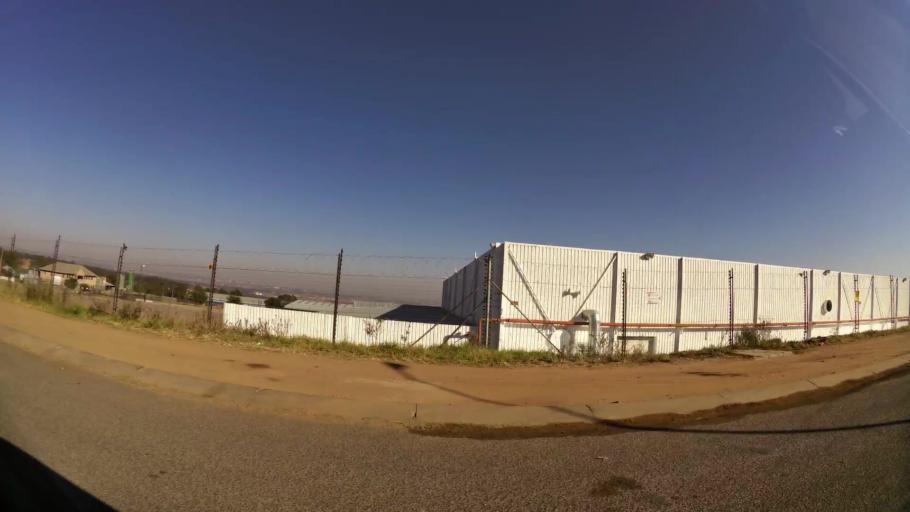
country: ZA
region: Gauteng
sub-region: City of Johannesburg Metropolitan Municipality
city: Modderfontein
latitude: -26.0619
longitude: 28.1743
